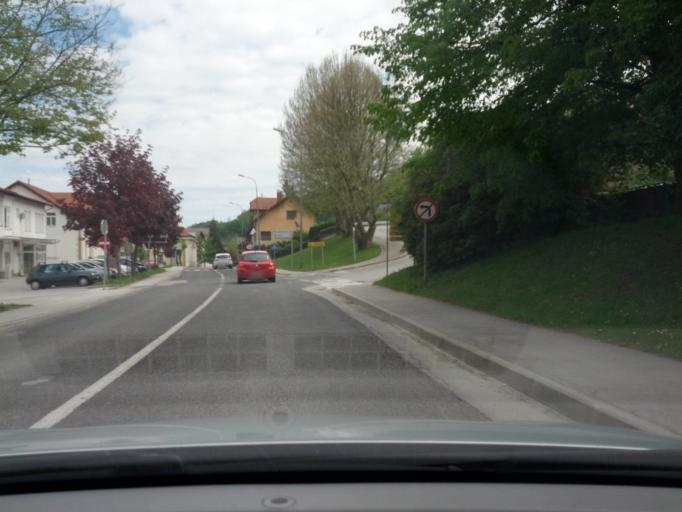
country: SI
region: Smarje pri Jelsah
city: Smarje pri Jelsah
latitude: 46.2293
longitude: 15.5155
